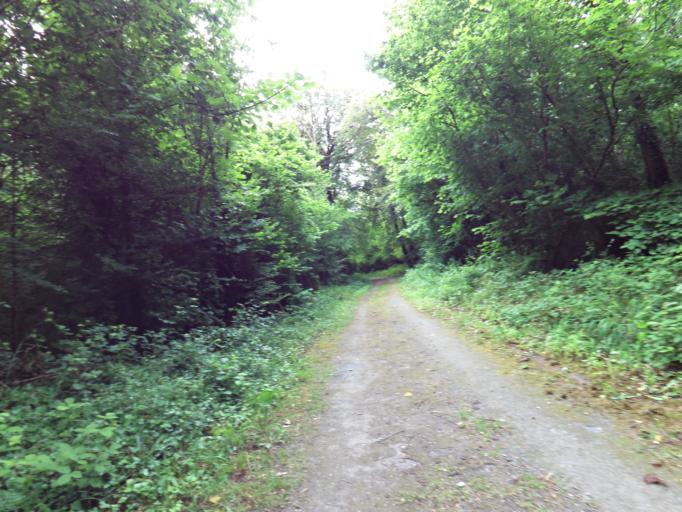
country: IE
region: Connaught
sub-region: County Galway
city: Gort
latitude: 53.0783
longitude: -8.8719
